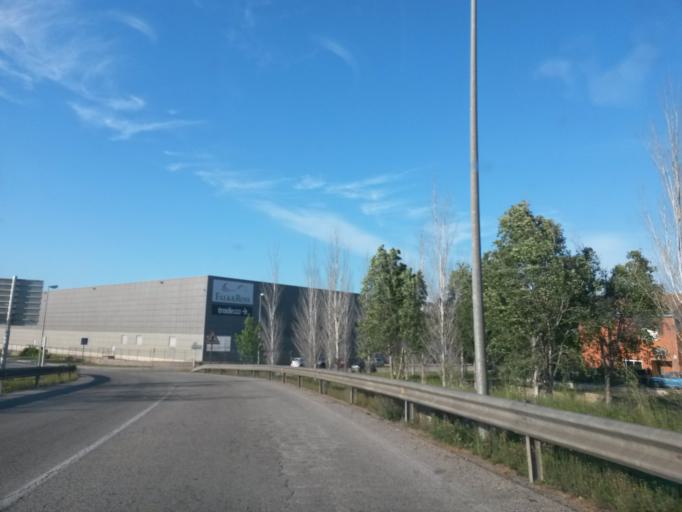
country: ES
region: Catalonia
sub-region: Provincia de Girona
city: Sant Julia de Ramis
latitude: 42.0278
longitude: 2.8687
